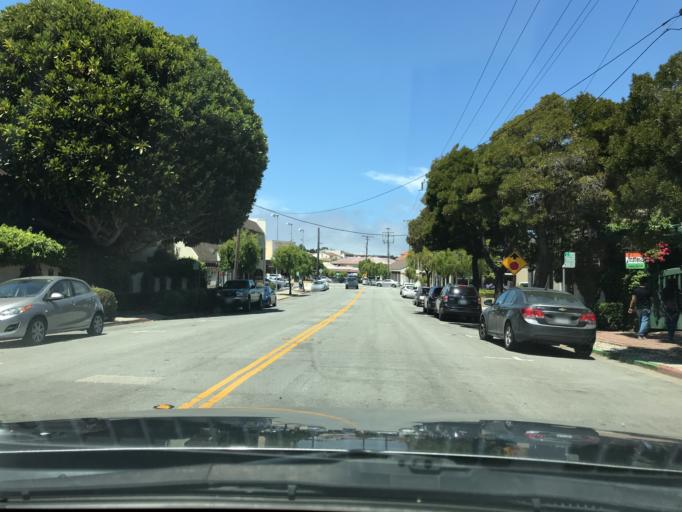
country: US
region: California
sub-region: Monterey County
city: Monterey
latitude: 36.5969
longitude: -121.8924
